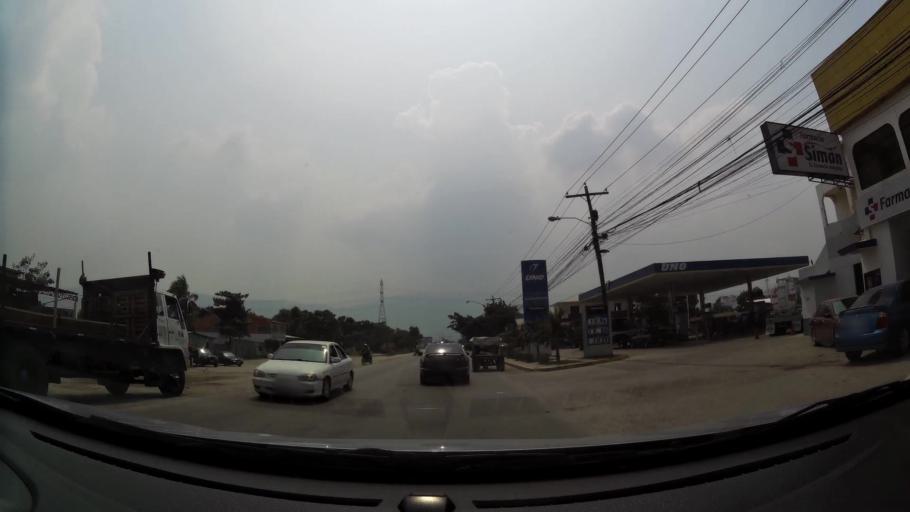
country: HN
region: Cortes
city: San Pedro Sula
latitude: 15.4715
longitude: -88.0004
